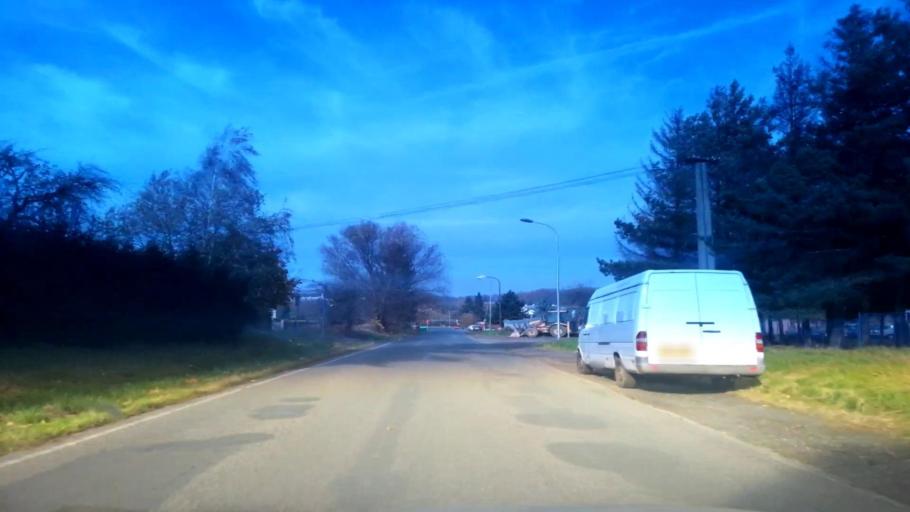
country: CZ
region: Karlovarsky
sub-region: Okres Cheb
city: Cheb
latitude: 50.0733
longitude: 12.3874
